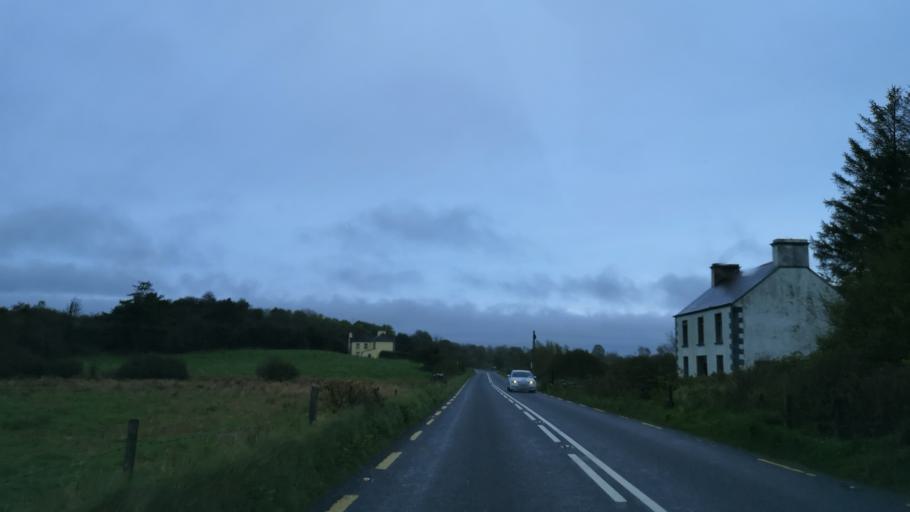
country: IE
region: Connaught
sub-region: Maigh Eo
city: Ballyhaunis
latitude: 53.7687
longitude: -8.7635
